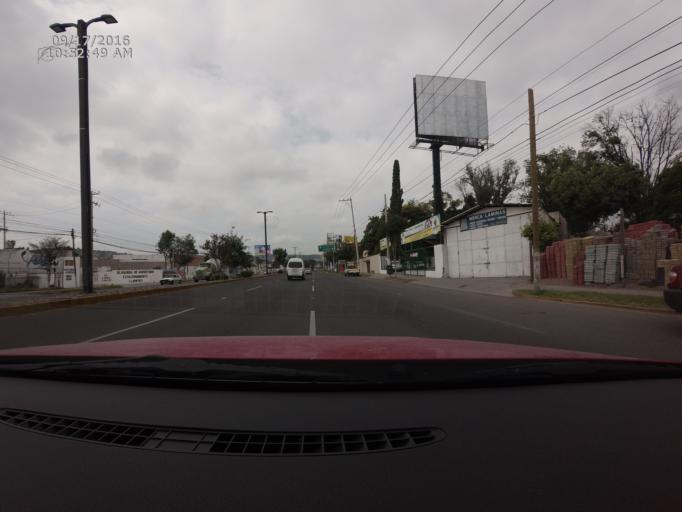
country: MX
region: Queretaro
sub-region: Corregidora
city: El Pueblito
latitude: 20.5354
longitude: -100.4367
